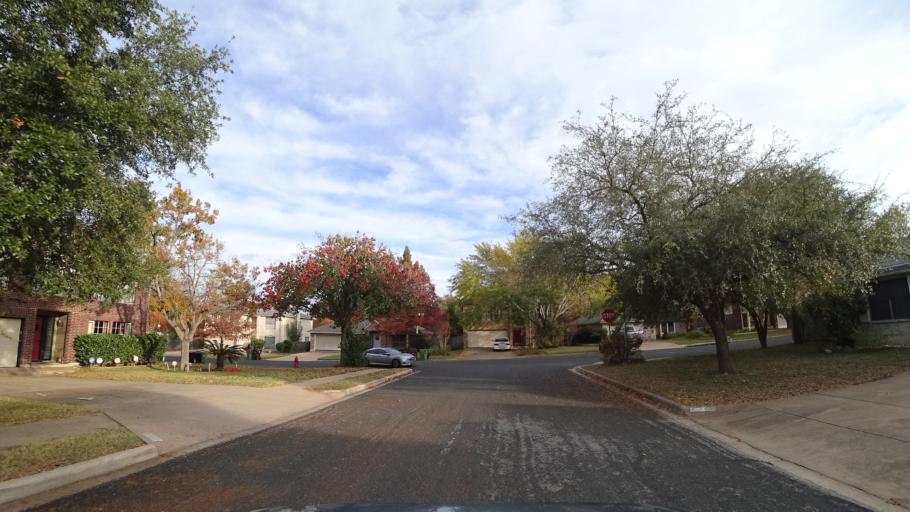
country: US
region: Texas
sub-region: Williamson County
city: Brushy Creek
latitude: 30.5157
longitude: -97.7246
